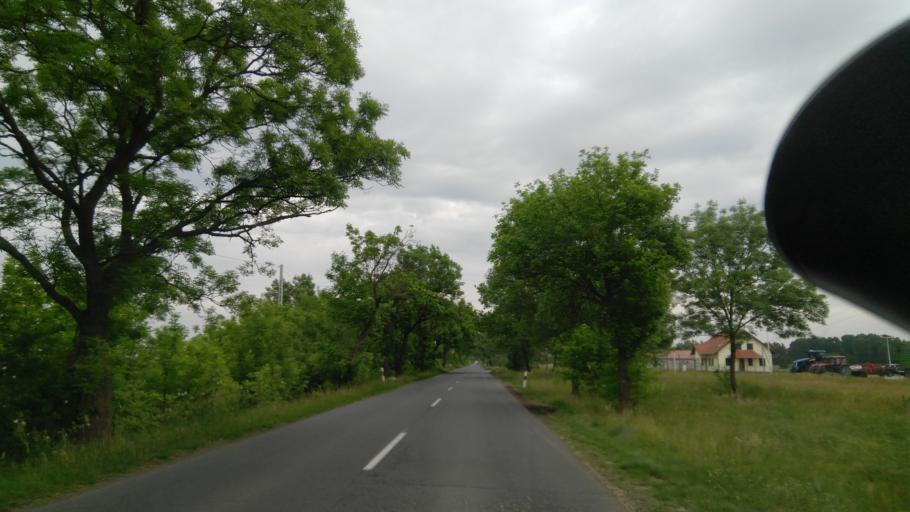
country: HU
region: Bekes
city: Veszto
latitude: 46.8939
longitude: 21.2467
